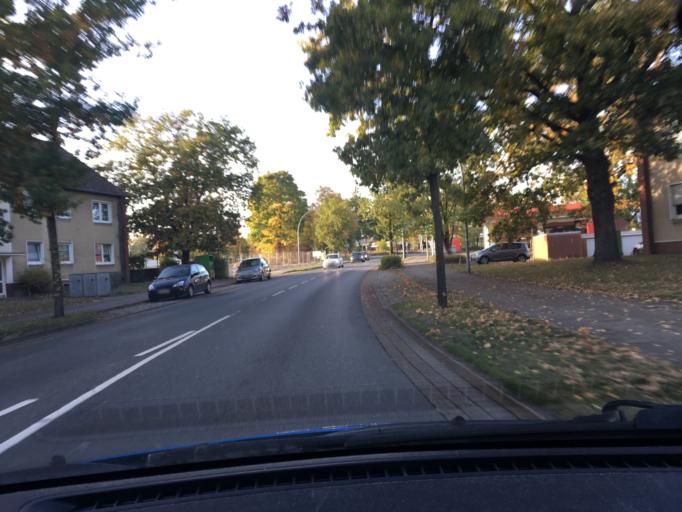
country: DE
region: Lower Saxony
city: Munster
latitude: 52.9884
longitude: 10.0820
